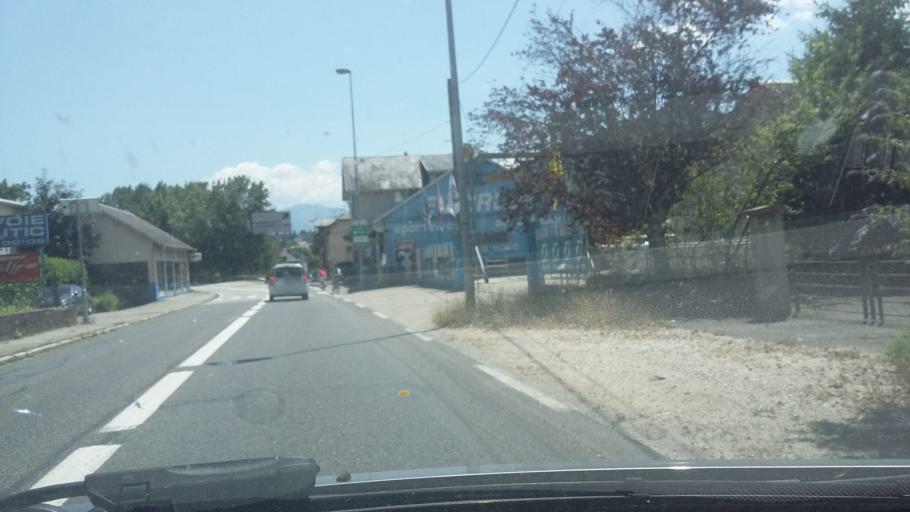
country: FR
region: Rhone-Alpes
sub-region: Departement de la Savoie
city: Le Bourget-du-Lac
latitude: 45.6537
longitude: 5.8588
